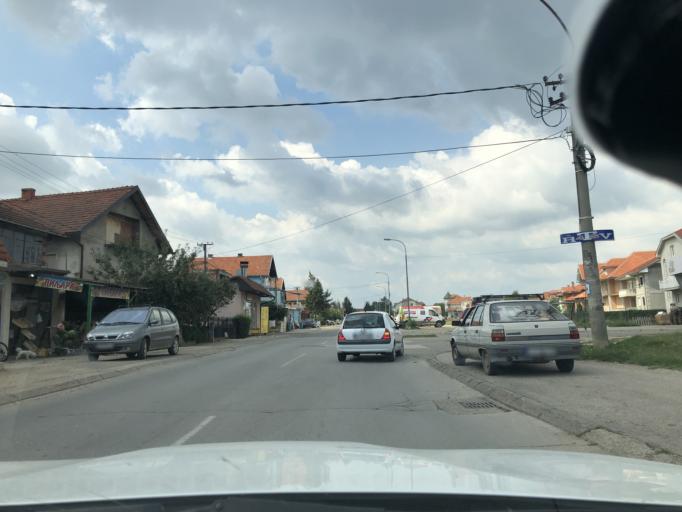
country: RS
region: Central Serbia
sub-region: Jablanicki Okrug
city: Leskovac
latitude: 42.9913
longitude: 21.9292
